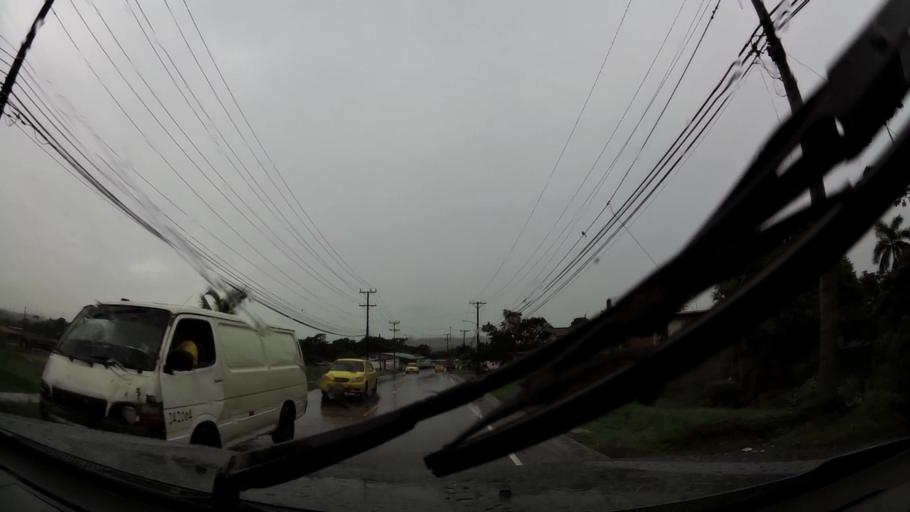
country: PA
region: Colon
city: Puerto Pilon
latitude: 9.3577
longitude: -79.7947
